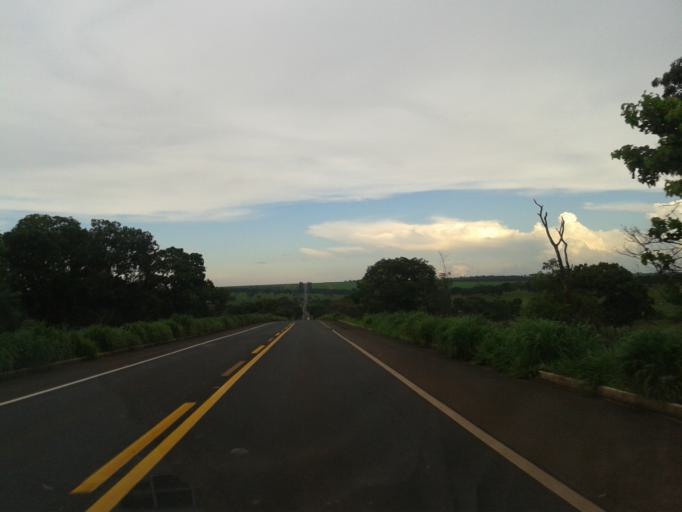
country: BR
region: Minas Gerais
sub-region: Santa Vitoria
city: Santa Vitoria
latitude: -18.9095
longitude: -50.2161
